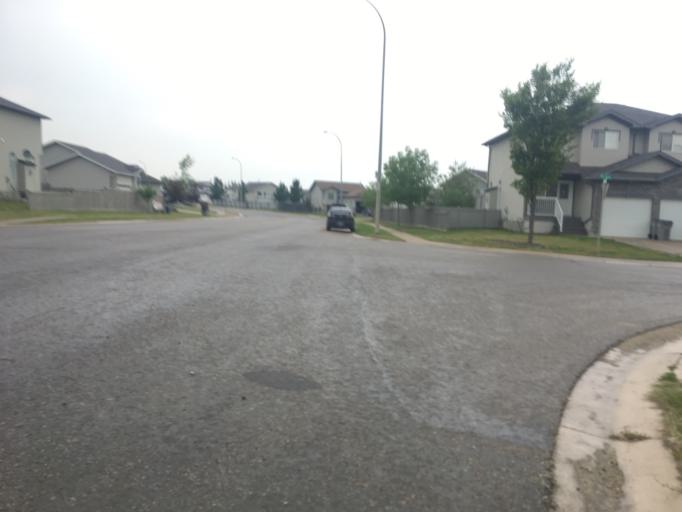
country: CA
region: Alberta
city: Grande Prairie
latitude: 55.1435
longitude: -118.8024
